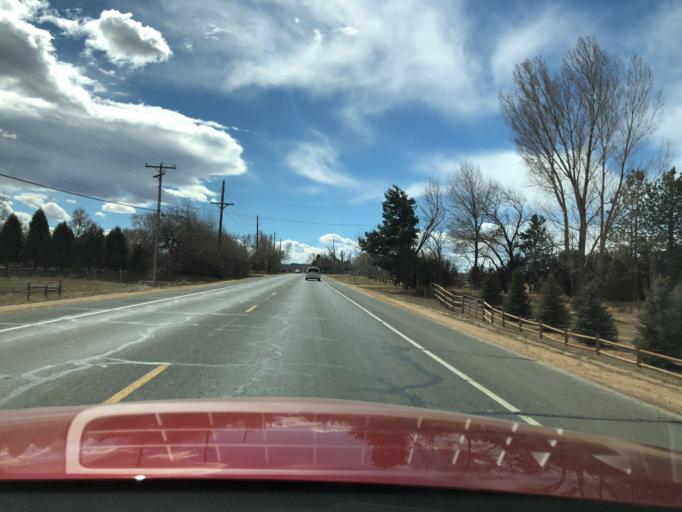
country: US
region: Colorado
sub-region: Boulder County
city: Gunbarrel
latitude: 40.0213
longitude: -105.1784
